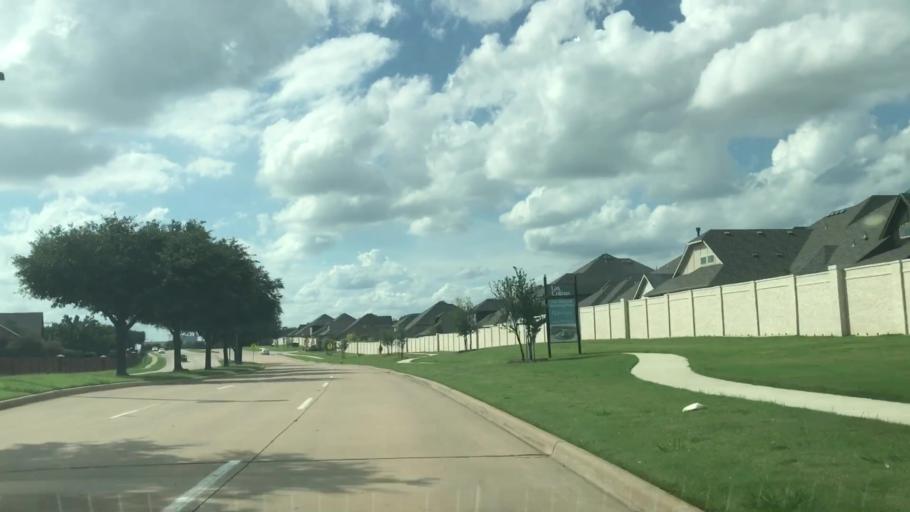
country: US
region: Texas
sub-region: Dallas County
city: Coppell
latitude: 32.9165
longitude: -96.9730
